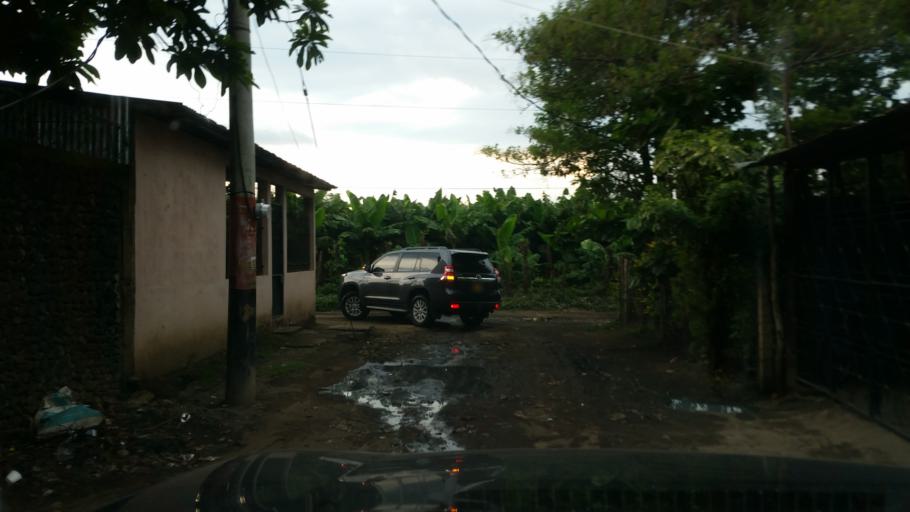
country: NI
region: Chinandega
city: Puerto Morazan
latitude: 12.7663
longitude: -87.1280
